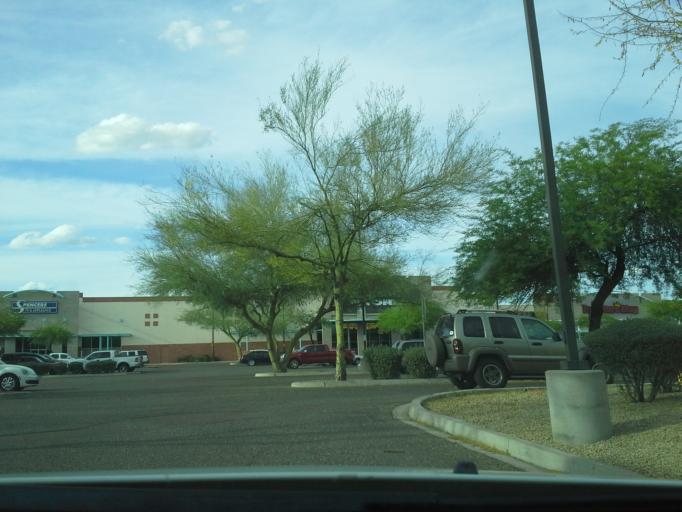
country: US
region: Arizona
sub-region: Maricopa County
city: Peoria
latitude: 33.6387
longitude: -112.2170
